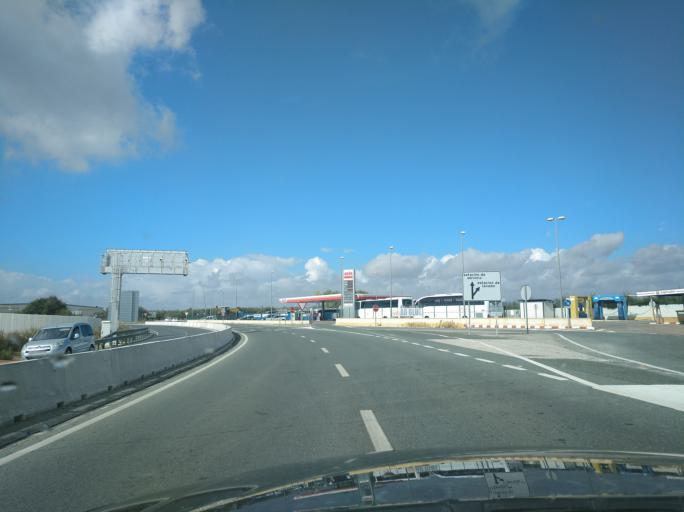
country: ES
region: Andalusia
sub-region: Provincia de Sevilla
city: Umbrete
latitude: 37.3619
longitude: -6.1431
